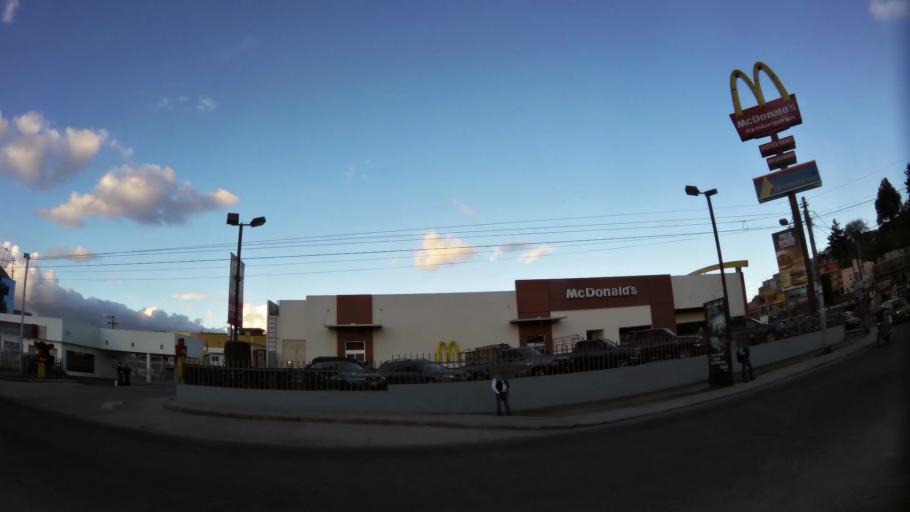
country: GT
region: Quetzaltenango
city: Quetzaltenango
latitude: 14.8388
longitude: -91.5076
